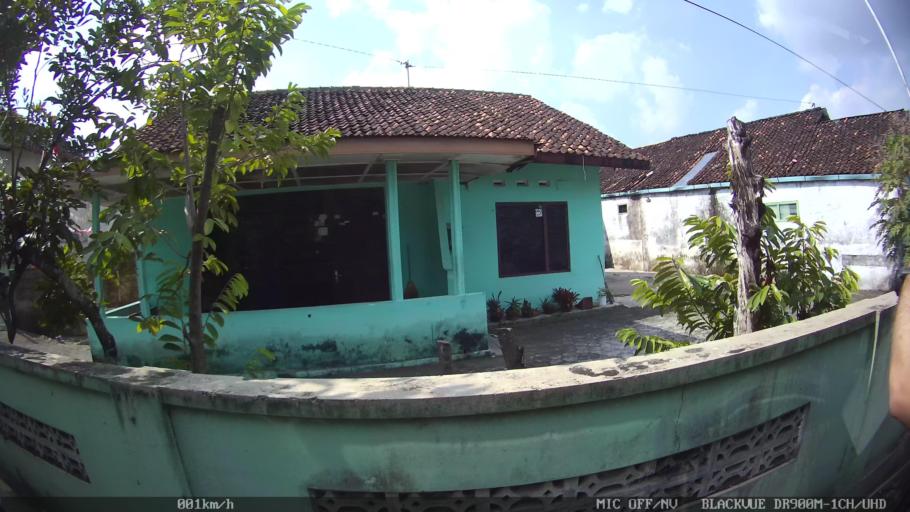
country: ID
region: Daerah Istimewa Yogyakarta
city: Yogyakarta
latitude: -7.8254
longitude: 110.3915
